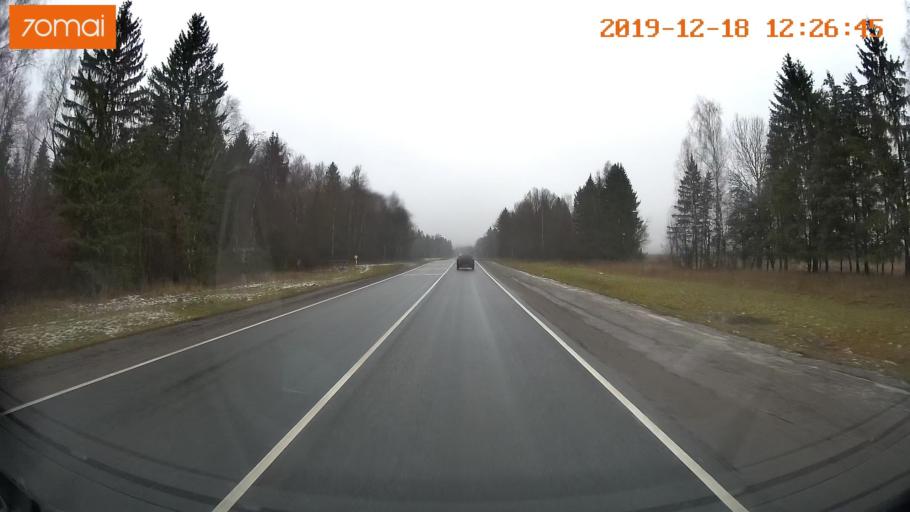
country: RU
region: Moskovskaya
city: Novopetrovskoye
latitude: 56.0546
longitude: 36.5020
